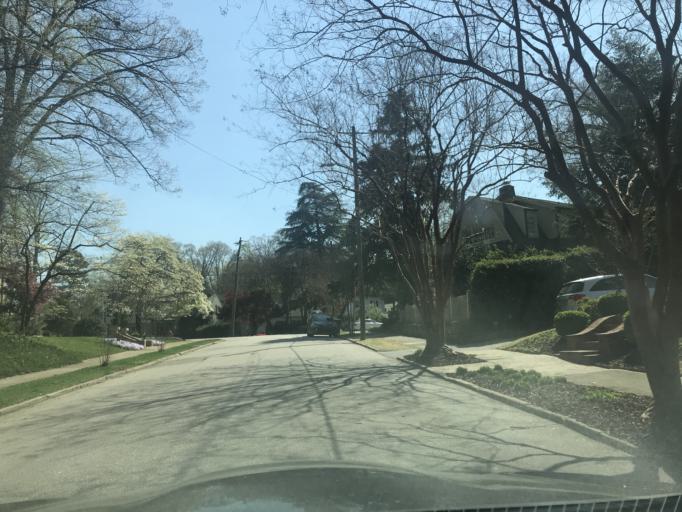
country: US
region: North Carolina
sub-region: Wake County
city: West Raleigh
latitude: 35.8125
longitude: -78.6428
